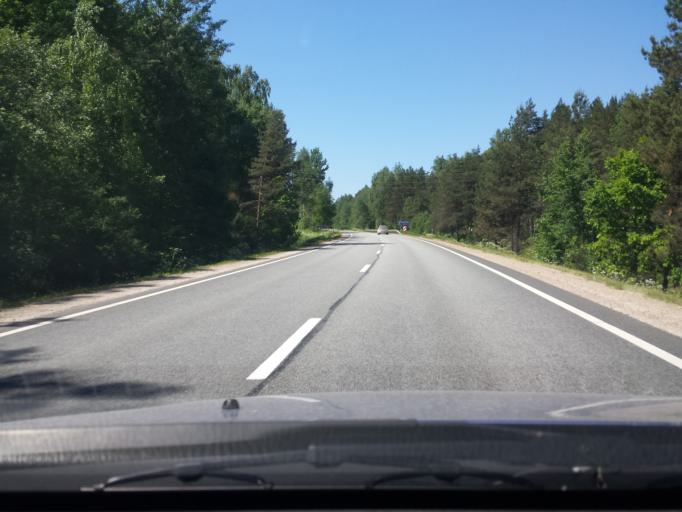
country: LV
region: Riga
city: Bergi
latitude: 56.9648
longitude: 24.3680
